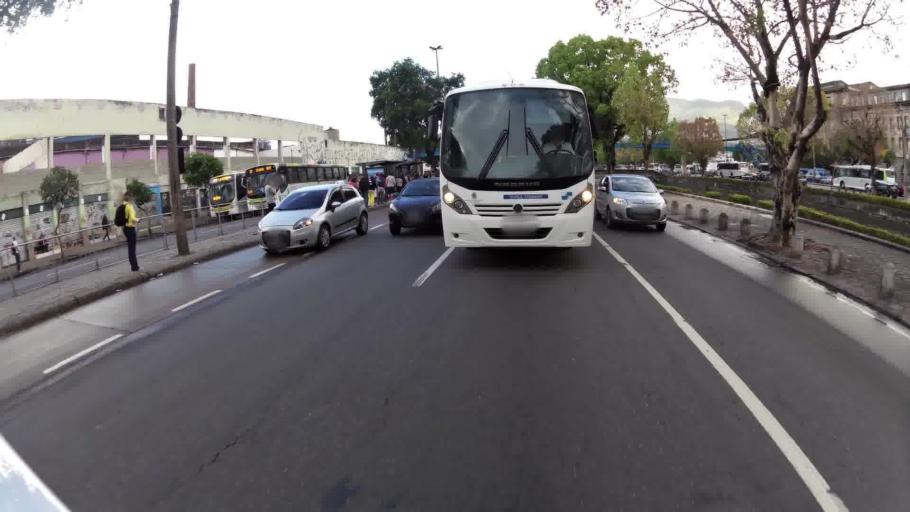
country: BR
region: Rio de Janeiro
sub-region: Rio De Janeiro
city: Rio de Janeiro
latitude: -22.9069
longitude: -43.2096
